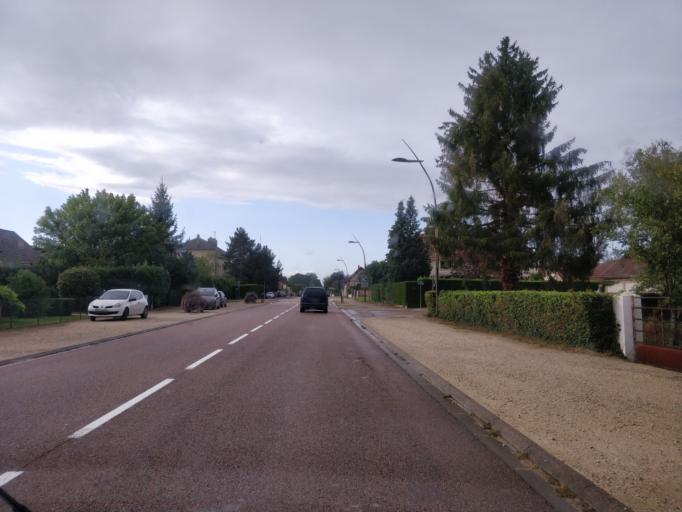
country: FR
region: Champagne-Ardenne
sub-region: Departement de l'Aube
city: Lusigny-sur-Barse
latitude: 48.2492
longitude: 4.2662
